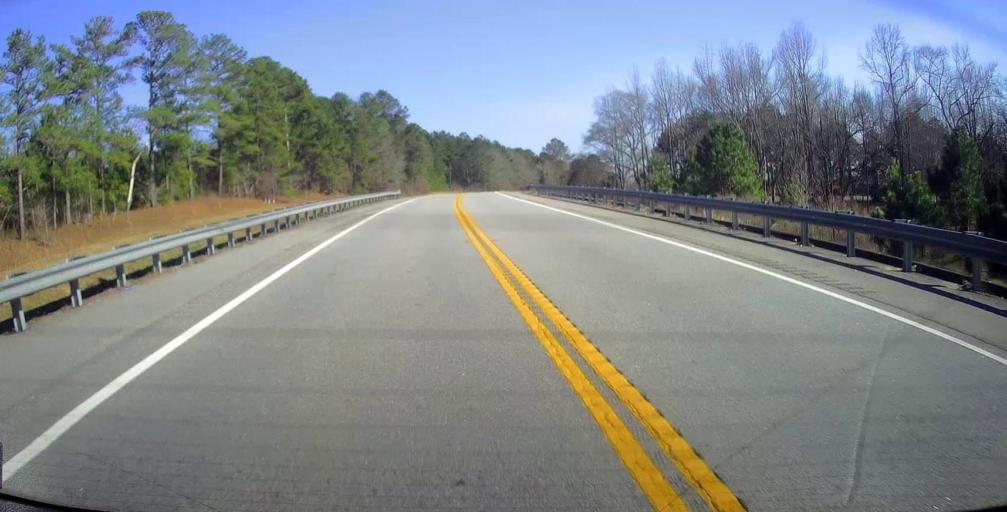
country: US
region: Georgia
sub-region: Macon County
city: Oglethorpe
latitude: 32.3443
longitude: -84.1356
